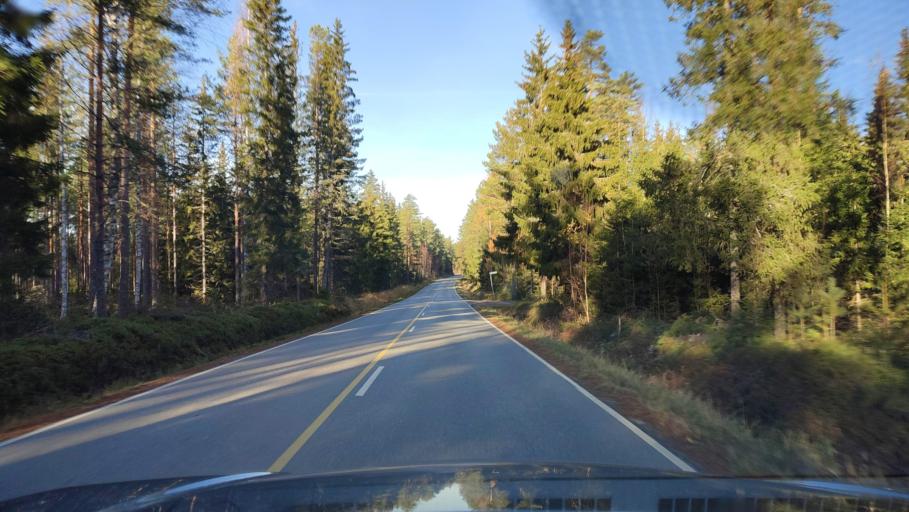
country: FI
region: Southern Ostrobothnia
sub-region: Suupohja
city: Karijoki
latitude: 62.2620
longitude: 21.7338
